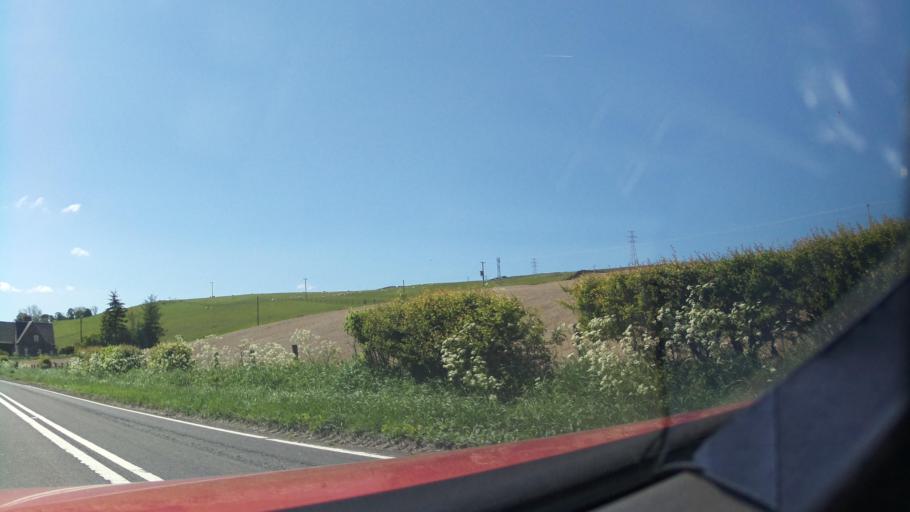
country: GB
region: Scotland
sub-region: The Scottish Borders
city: Hawick
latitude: 55.3725
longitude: -2.8782
